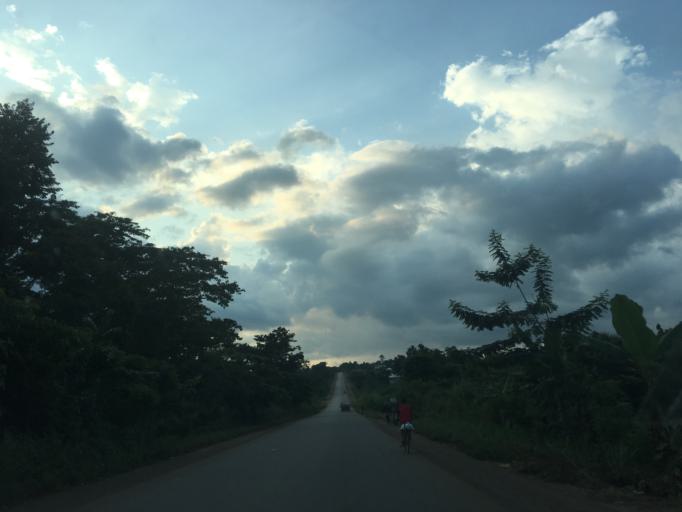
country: GH
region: Western
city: Bibiani
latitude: 6.7050
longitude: -2.4508
